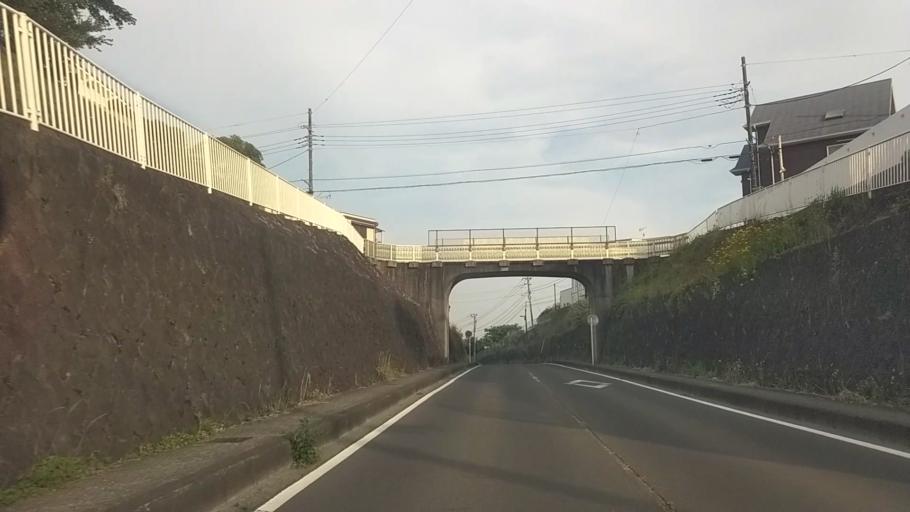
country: JP
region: Kanagawa
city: Odawara
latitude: 35.3123
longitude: 139.1173
